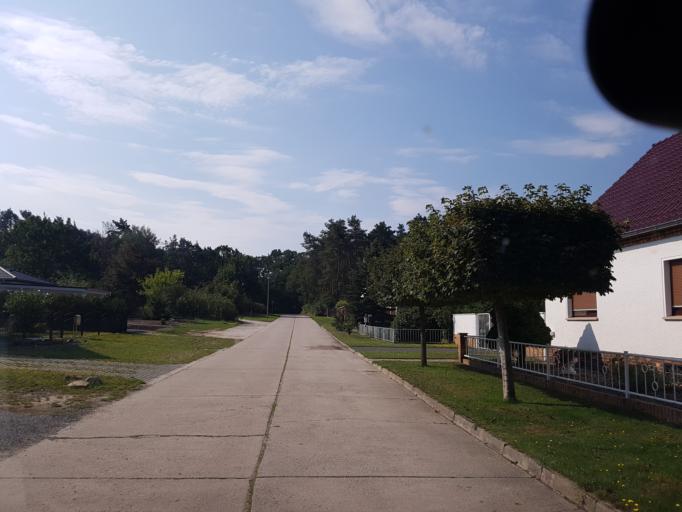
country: DE
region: Brandenburg
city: Plessa
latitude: 51.5309
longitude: 13.6655
